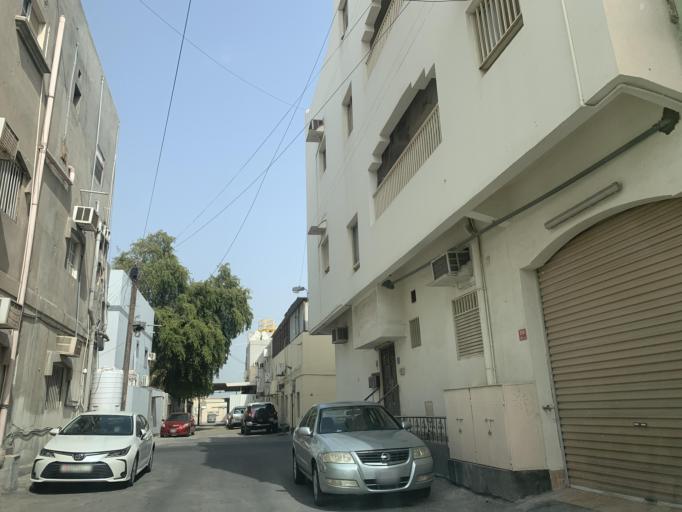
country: BH
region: Northern
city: Madinat `Isa
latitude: 26.1838
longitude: 50.5468
